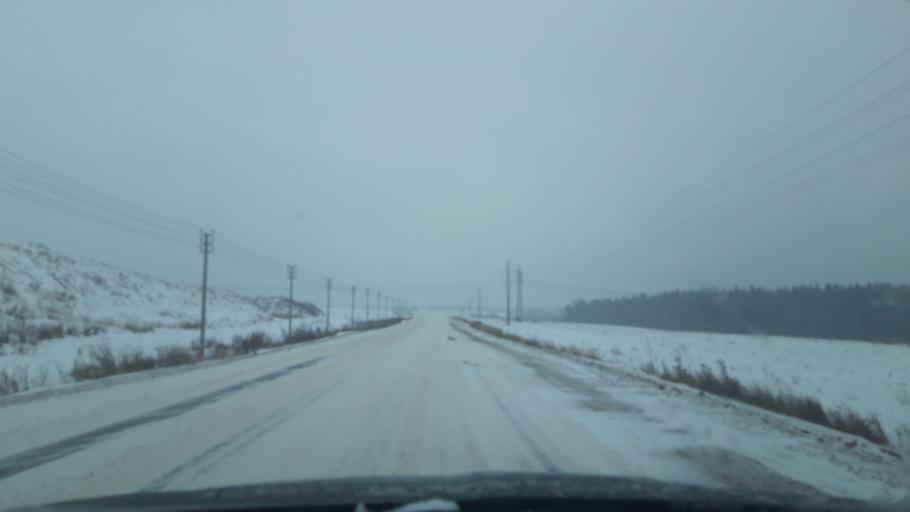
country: RU
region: Moskovskaya
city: Avtopoligon
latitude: 56.2616
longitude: 37.2292
